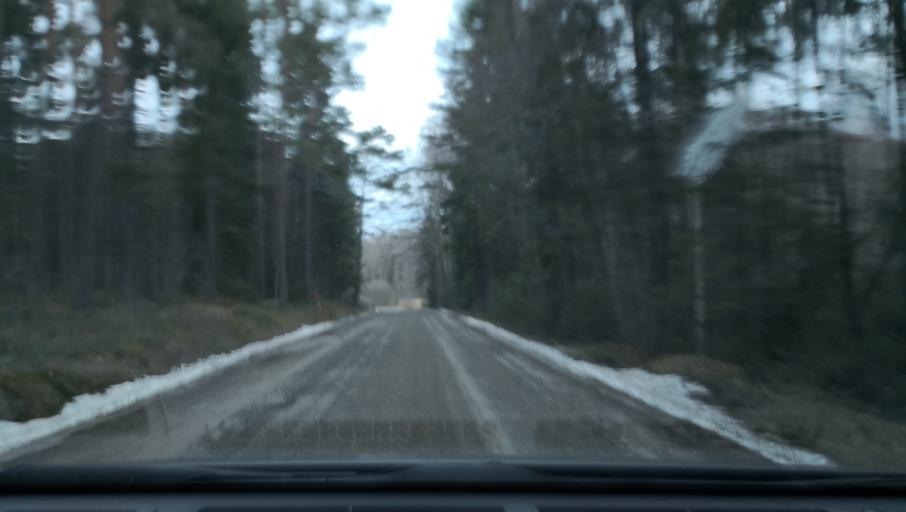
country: SE
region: Vaestmanland
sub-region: Kopings Kommun
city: Kolsva
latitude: 59.5796
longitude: 15.7135
